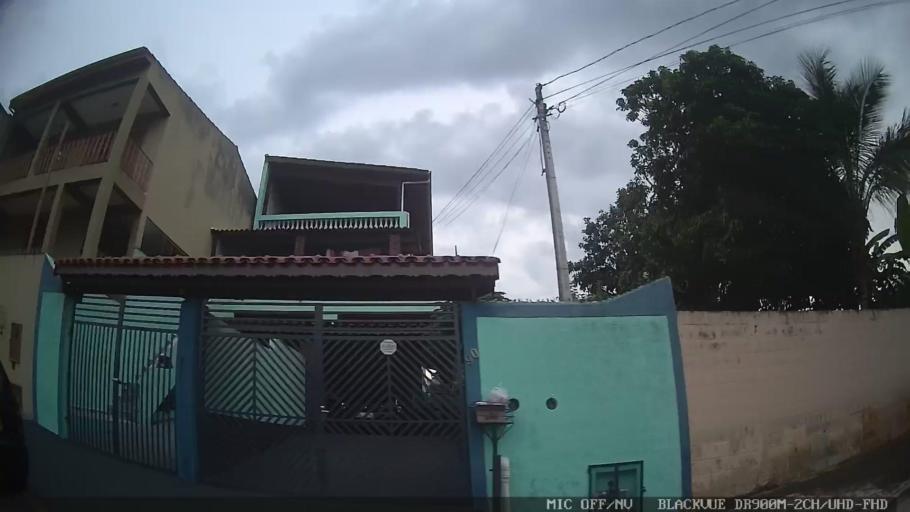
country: BR
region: Sao Paulo
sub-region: Atibaia
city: Atibaia
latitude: -23.1301
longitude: -46.5599
